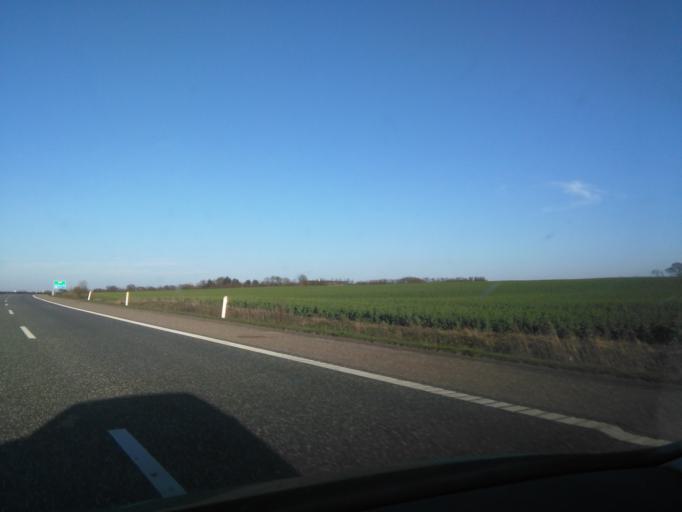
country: DK
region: Central Jutland
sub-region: Skanderborg Kommune
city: Galten
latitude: 56.1478
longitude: 9.8313
